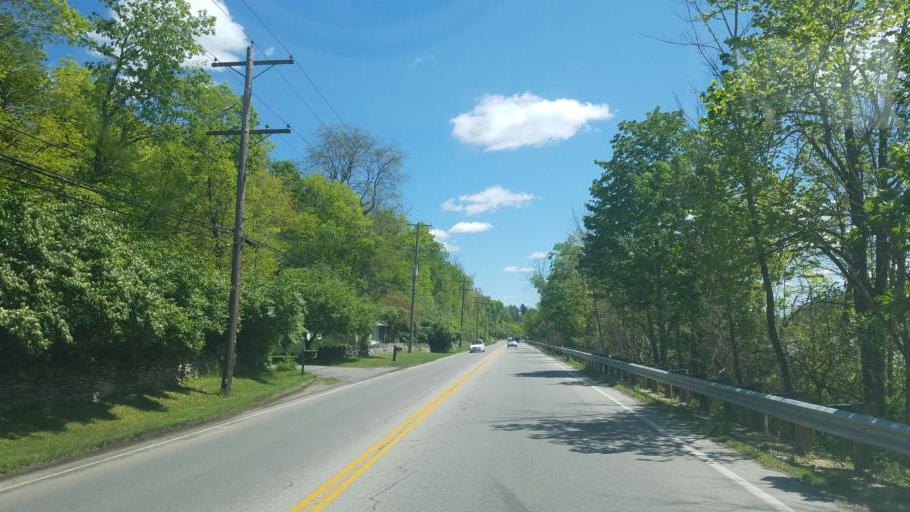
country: US
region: Ohio
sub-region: Franklin County
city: Dublin
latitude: 40.0578
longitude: -83.1000
